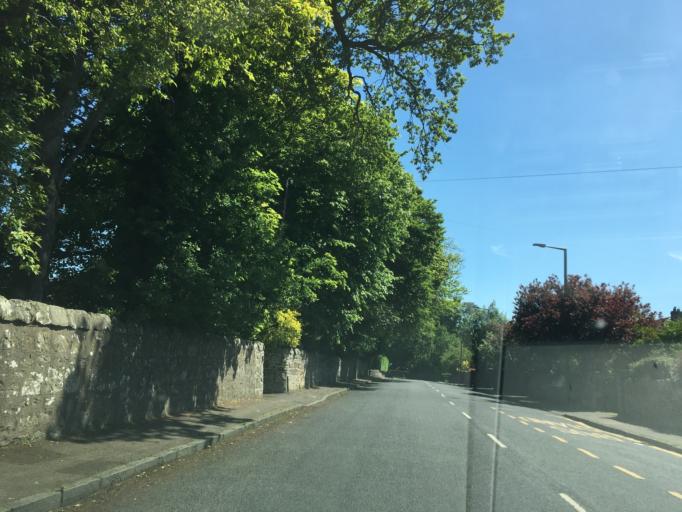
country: GB
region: Scotland
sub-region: Fife
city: Aberdour
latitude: 55.9736
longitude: -3.2963
